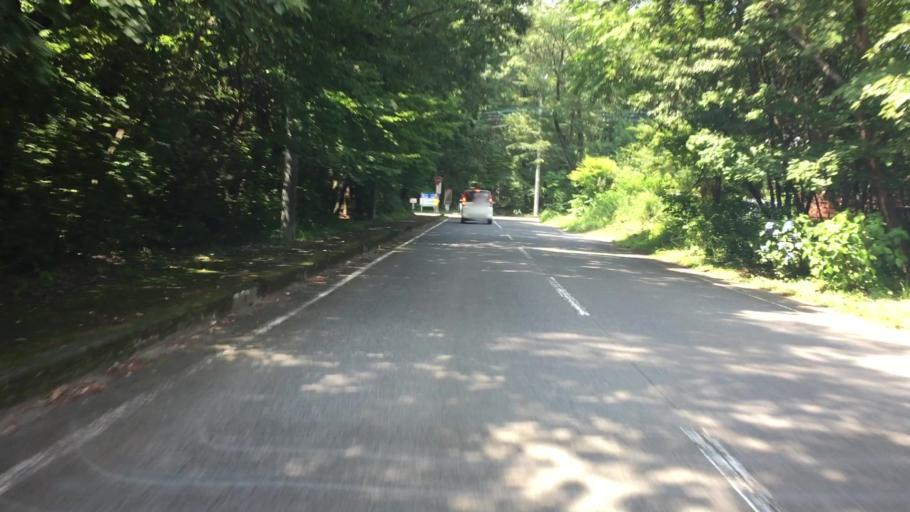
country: JP
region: Tochigi
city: Kuroiso
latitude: 36.9319
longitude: 139.9554
